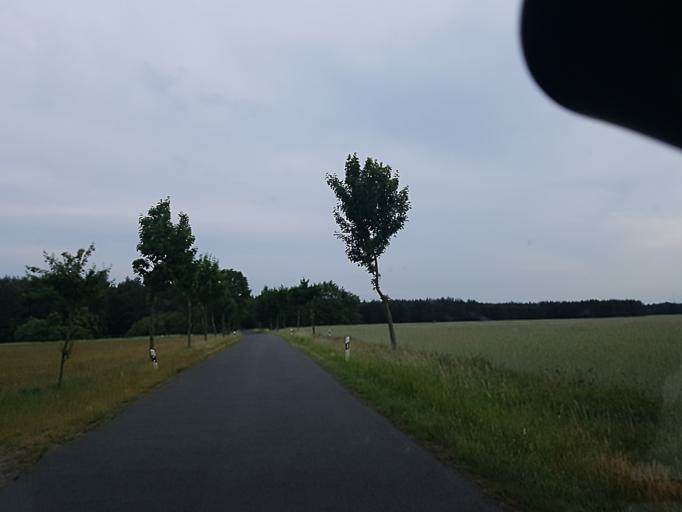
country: DE
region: Saxony-Anhalt
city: Holzdorf
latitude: 51.7754
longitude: 13.1129
